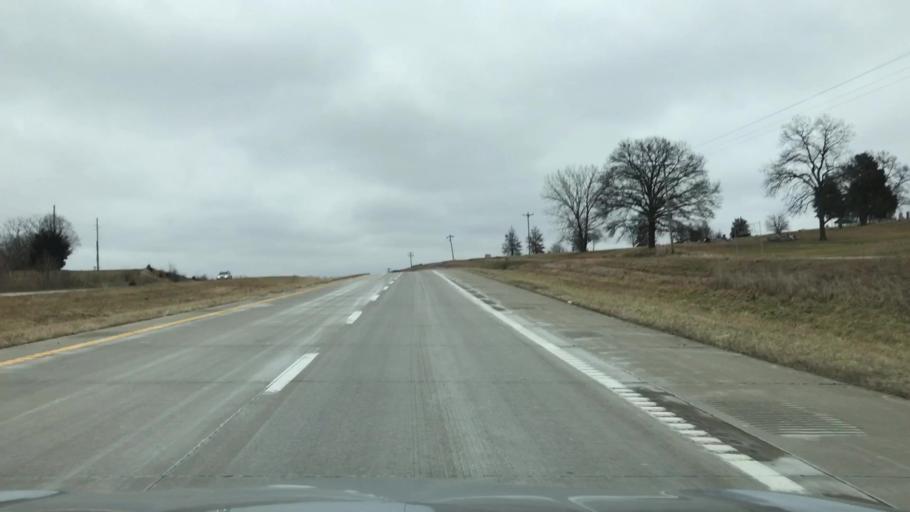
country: US
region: Missouri
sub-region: Livingston County
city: Chillicothe
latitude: 39.7385
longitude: -93.6368
